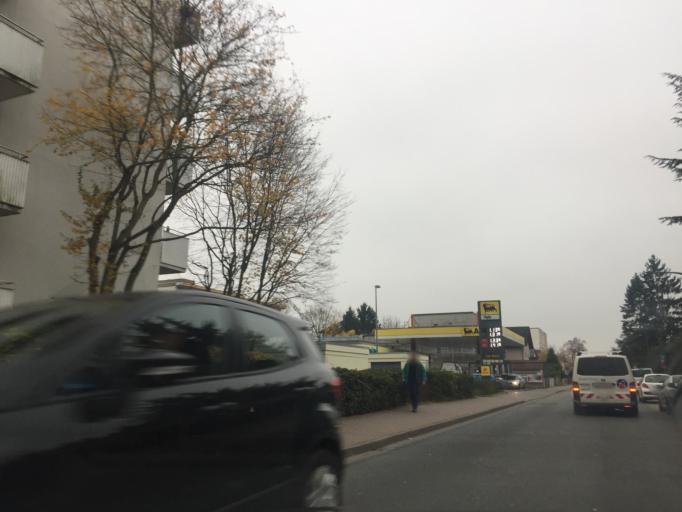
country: DE
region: Hesse
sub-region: Regierungsbezirk Darmstadt
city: Maintal
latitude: 50.1484
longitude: 8.8079
